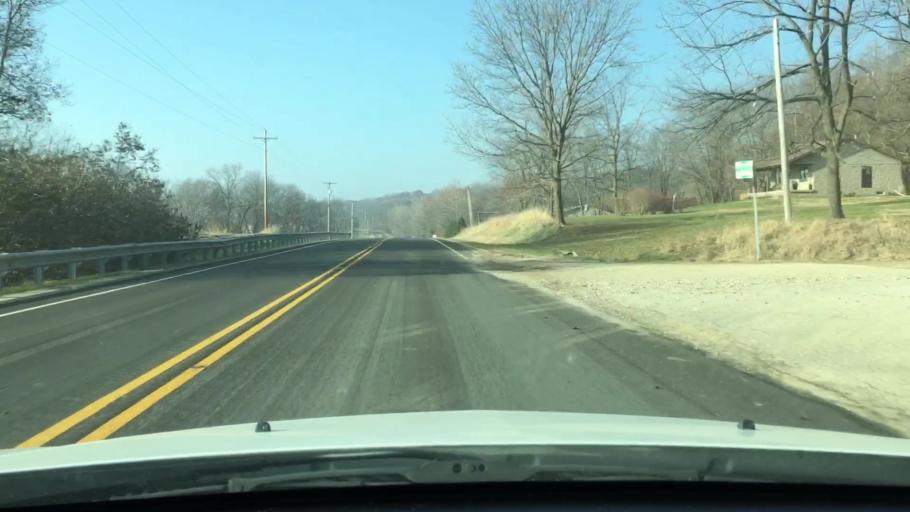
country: US
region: Illinois
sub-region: Mason County
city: Havana
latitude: 40.4203
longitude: -90.0024
